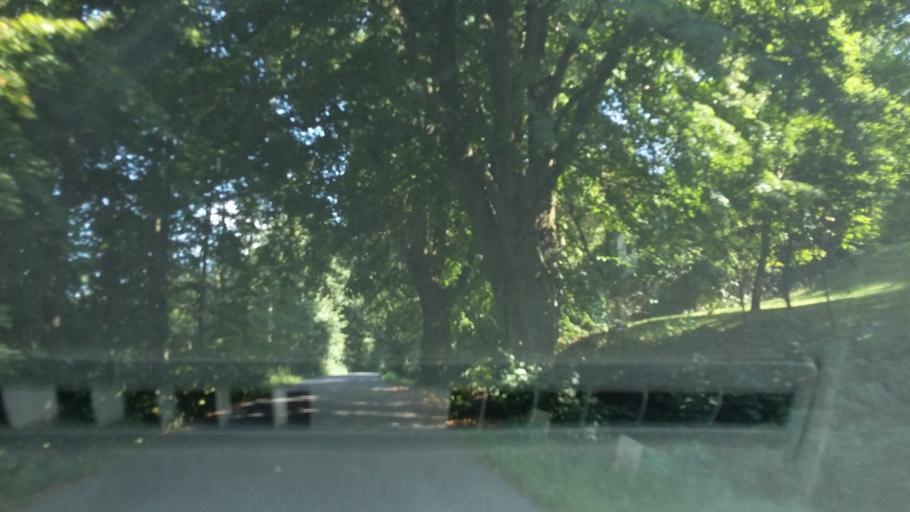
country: CZ
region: Liberecky
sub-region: Okres Semily
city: Turnov
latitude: 50.5989
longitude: 15.1773
